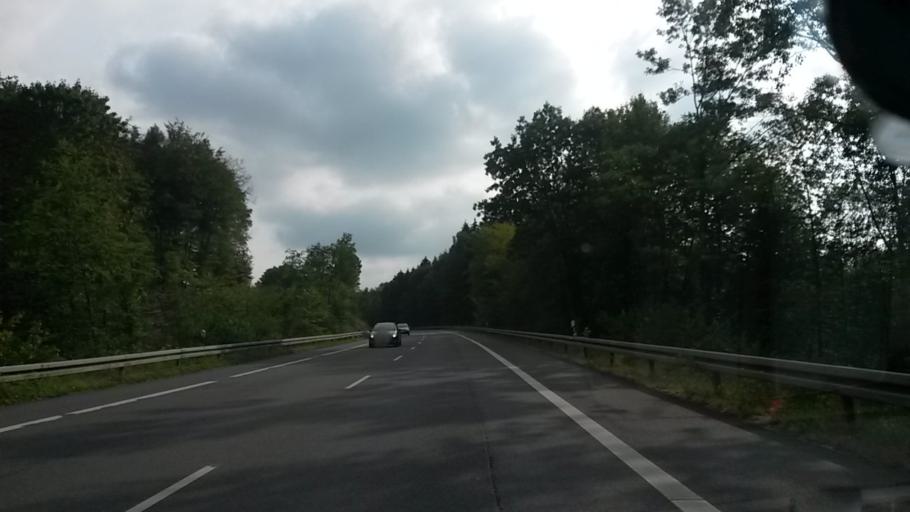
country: DE
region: North Rhine-Westphalia
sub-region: Regierungsbezirk Koln
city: Engelskirchen
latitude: 50.9989
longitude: 7.4289
